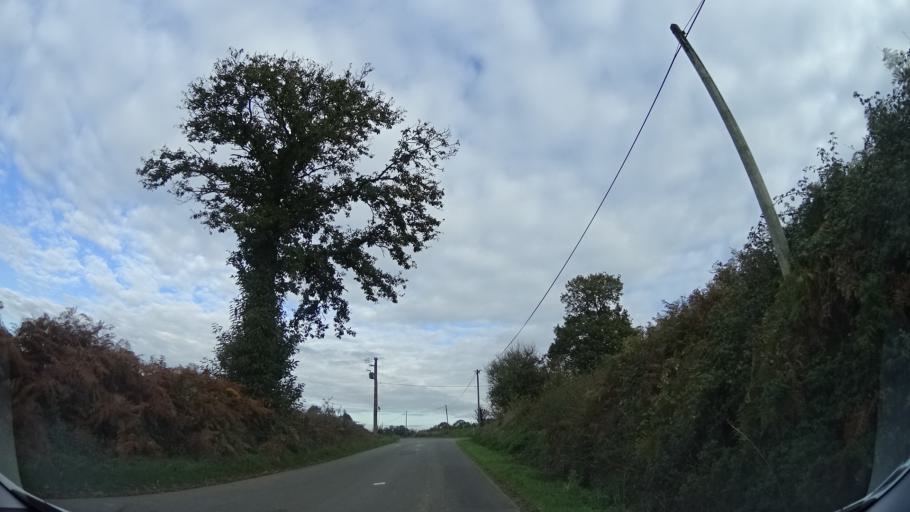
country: FR
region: Brittany
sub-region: Departement d'Ille-et-Vilaine
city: Geveze
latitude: 48.2308
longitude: -1.7866
